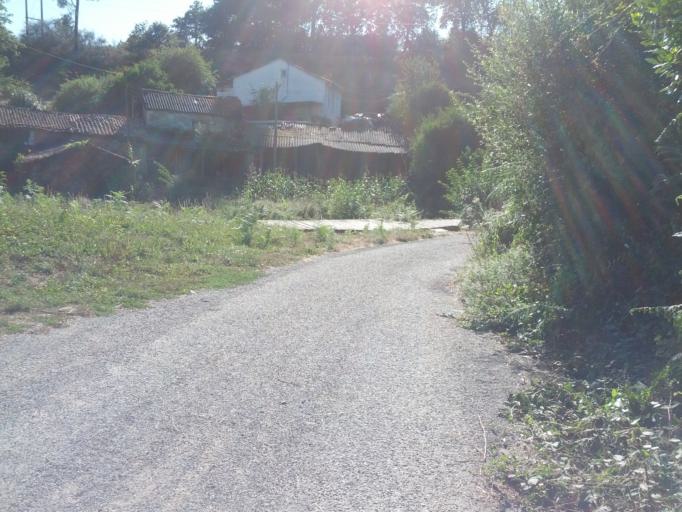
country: ES
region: Galicia
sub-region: Provincia da Coruna
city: Santiago de Compostela
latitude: 42.8778
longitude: -8.5632
